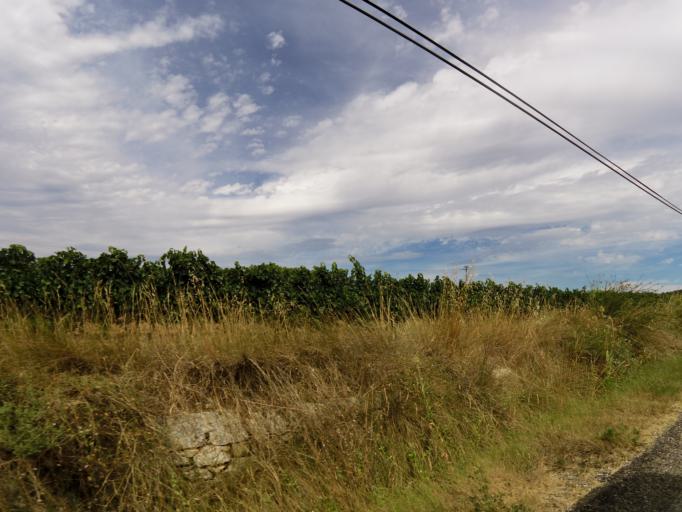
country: FR
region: Languedoc-Roussillon
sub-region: Departement du Gard
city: Villevieille
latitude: 43.8229
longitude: 4.1347
